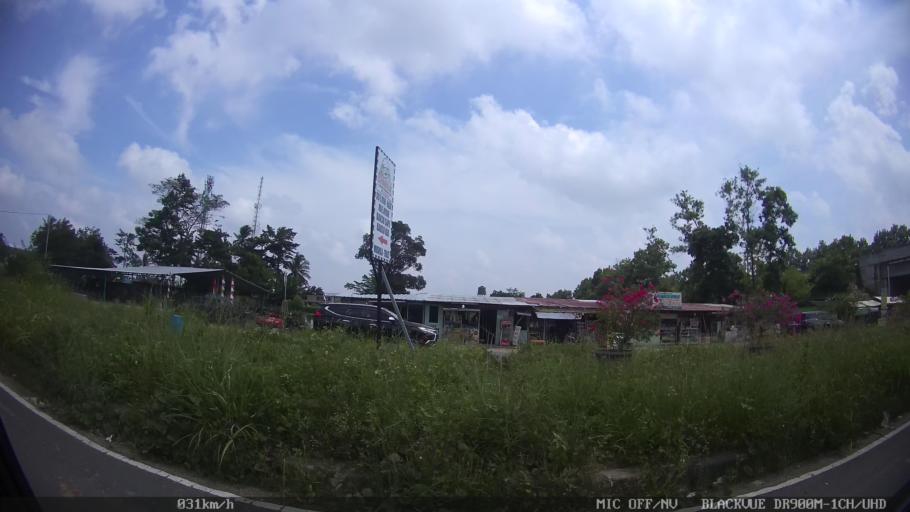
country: ID
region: Lampung
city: Kedaton
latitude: -5.3532
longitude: 105.3225
